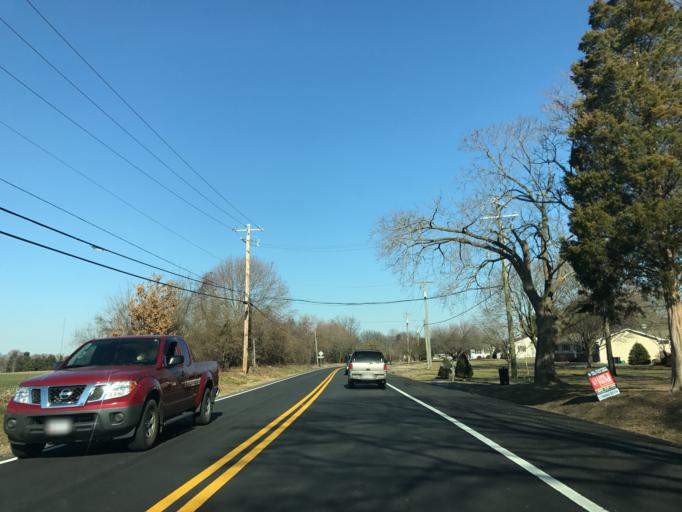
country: US
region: Maryland
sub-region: Queen Anne's County
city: Centreville
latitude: 39.0338
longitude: -76.0800
